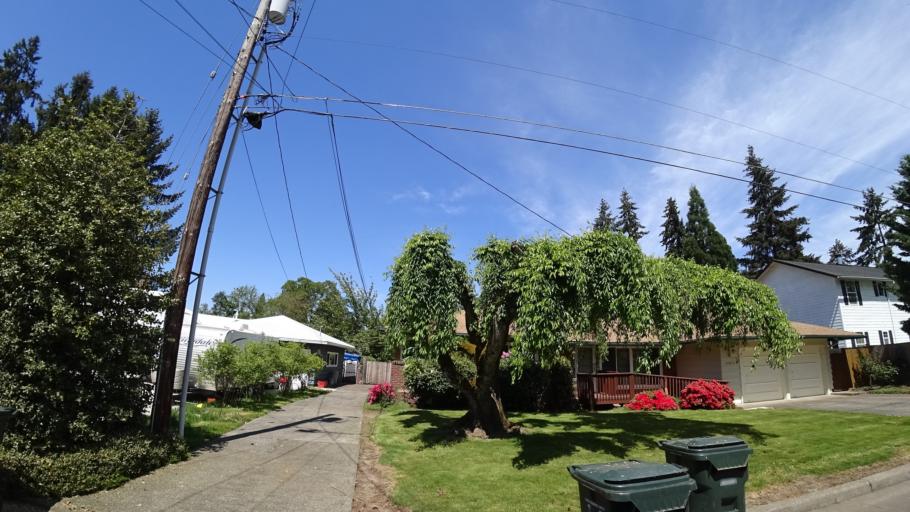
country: US
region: Oregon
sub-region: Washington County
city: Aloha
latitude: 45.4856
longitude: -122.8440
